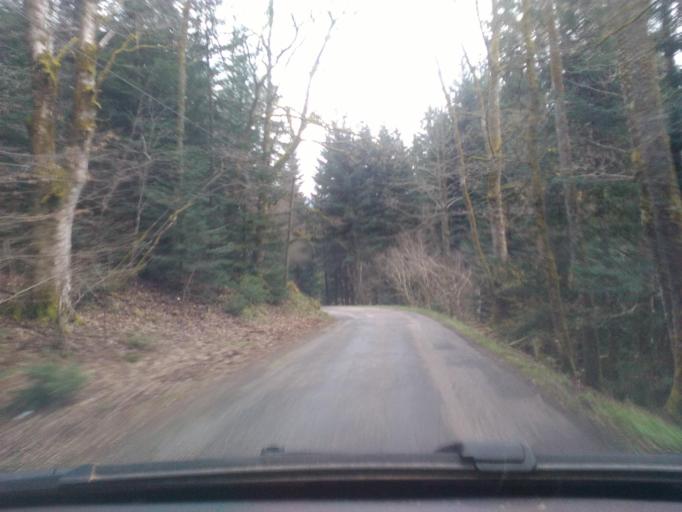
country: FR
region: Lorraine
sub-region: Departement des Vosges
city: Granges-sur-Vologne
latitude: 48.1370
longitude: 6.8217
